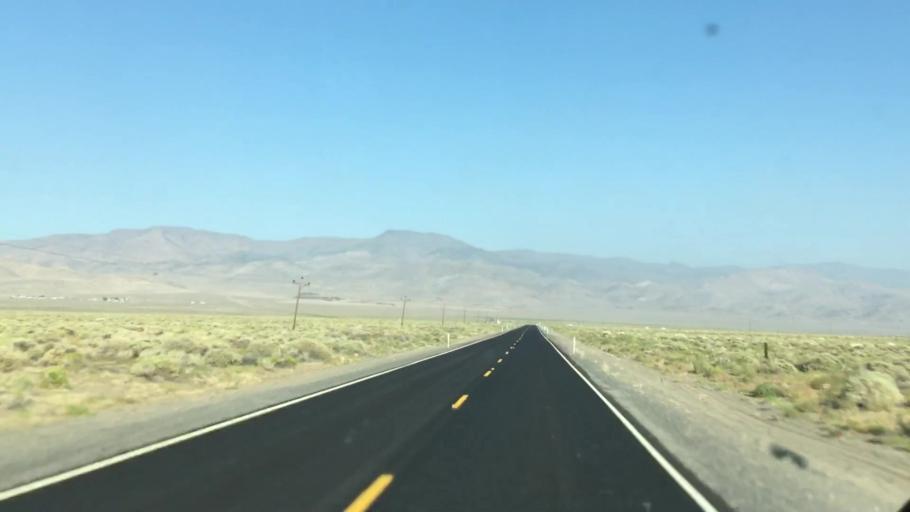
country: US
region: Nevada
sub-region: Lyon County
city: Fernley
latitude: 39.6466
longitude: -119.3139
